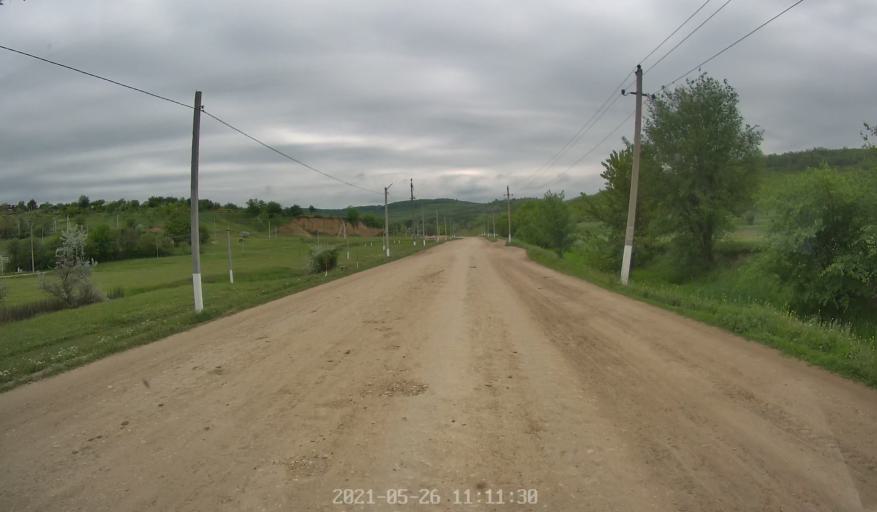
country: MD
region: Hincesti
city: Dancu
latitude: 46.8238
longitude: 28.3764
